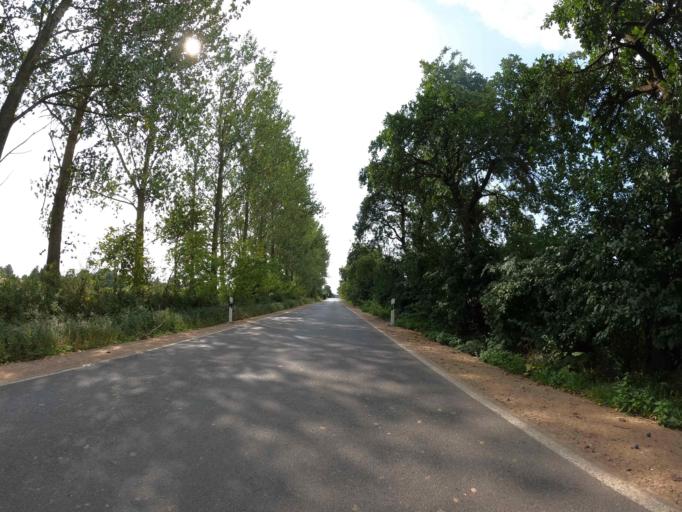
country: DE
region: Mecklenburg-Vorpommern
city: Malchow
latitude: 53.4385
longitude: 12.5025
